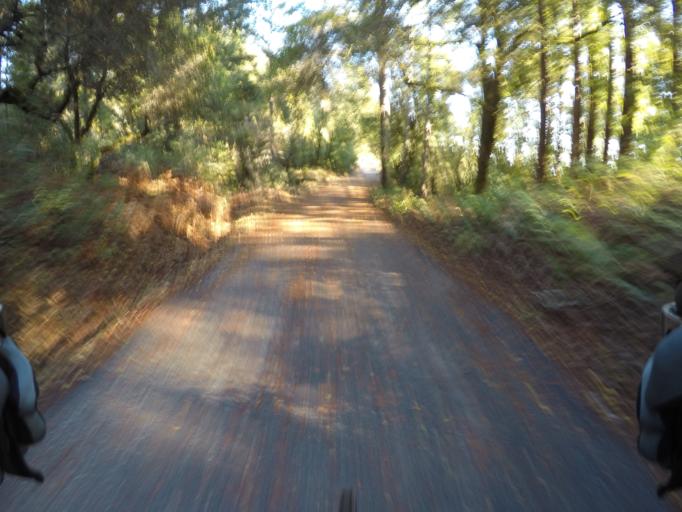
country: US
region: California
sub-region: Santa Cruz County
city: Mount Hermon
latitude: 37.0236
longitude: -122.0526
